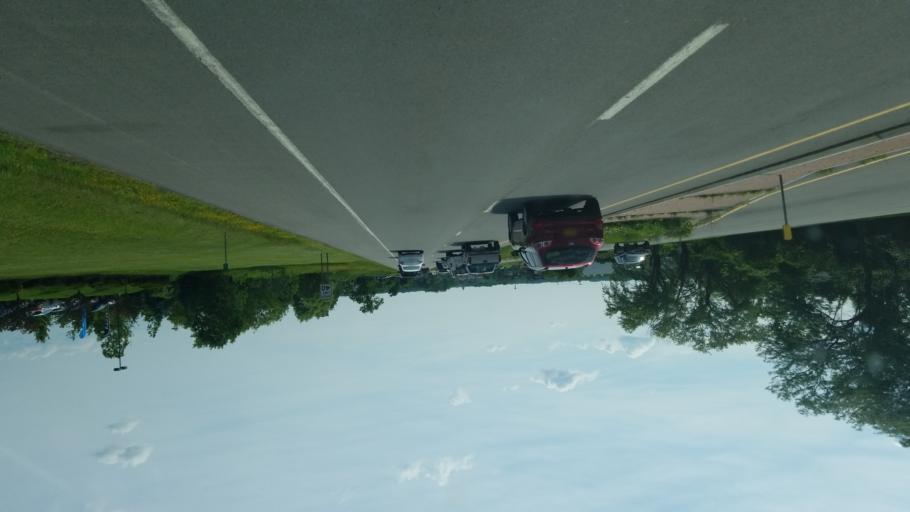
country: US
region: New York
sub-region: Ontario County
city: Canandaigua
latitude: 42.8729
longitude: -77.2414
